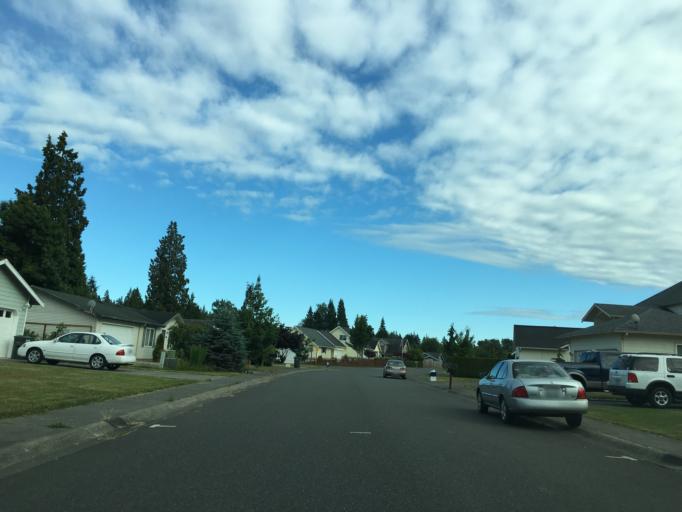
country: US
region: Washington
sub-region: Whatcom County
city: Birch Bay
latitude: 48.9487
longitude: -122.7401
